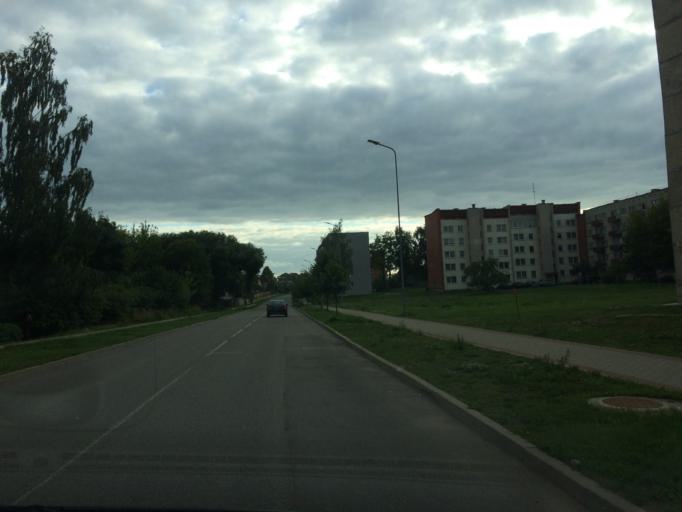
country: LV
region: Rezekne
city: Rezekne
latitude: 56.5172
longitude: 27.3335
